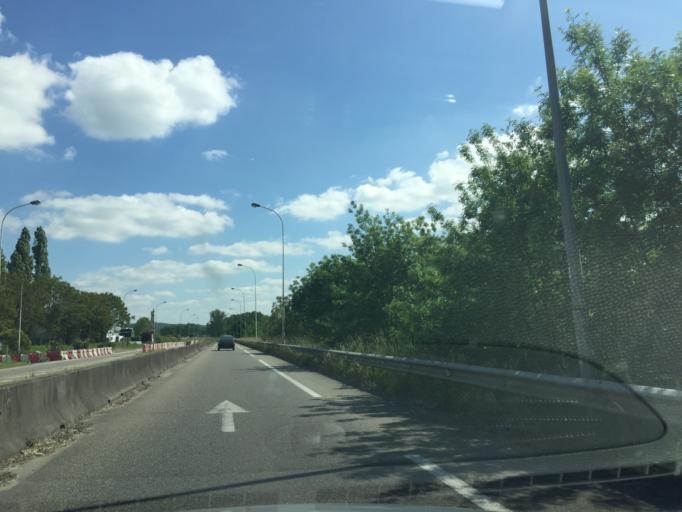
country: FR
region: Aquitaine
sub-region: Departement du Lot-et-Garonne
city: Le Passage
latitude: 44.1854
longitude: 0.6137
